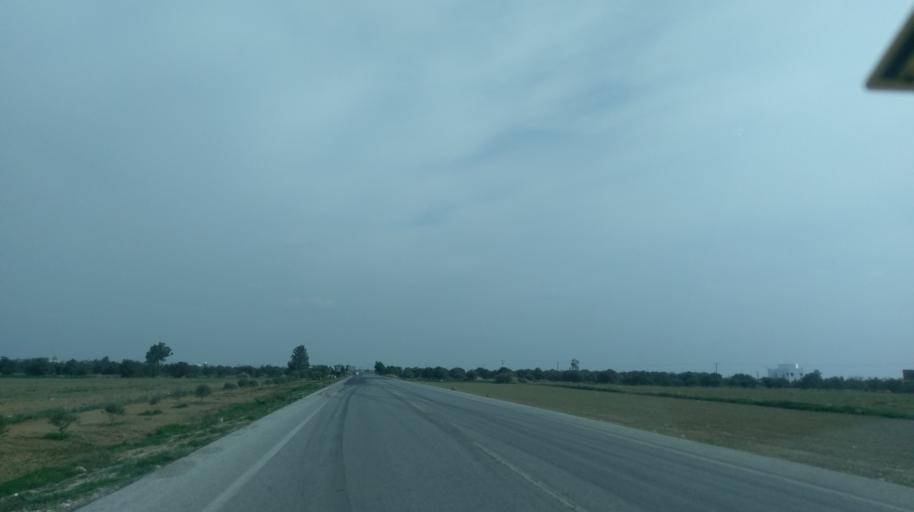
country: CY
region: Larnaka
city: Athienou
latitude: 35.2291
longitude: 33.5432
